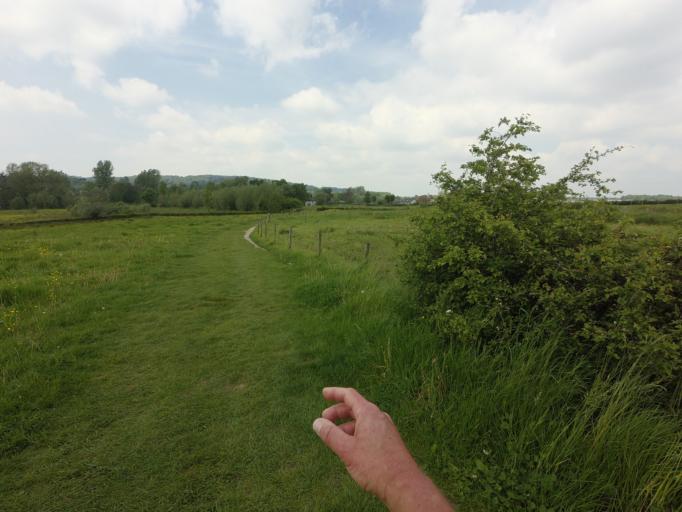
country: BE
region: Wallonia
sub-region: Province de Liege
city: Plombieres
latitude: 50.7834
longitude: 5.9223
